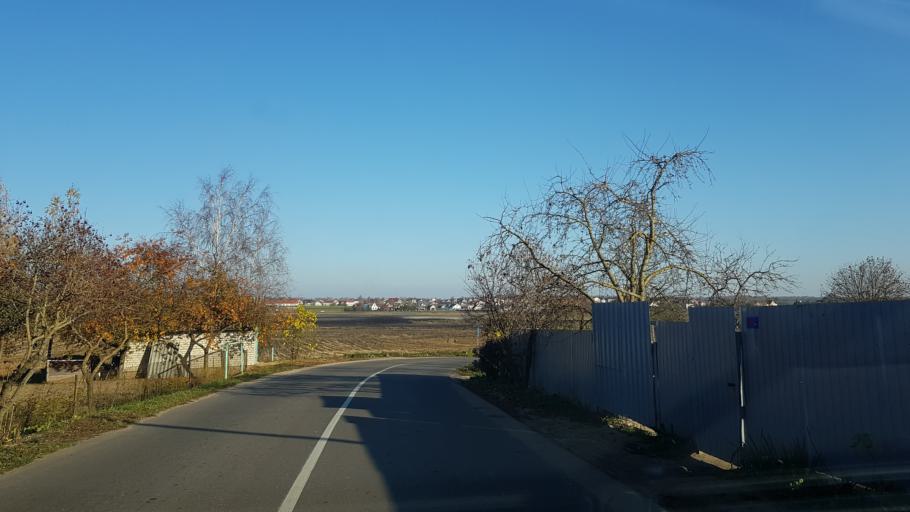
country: BY
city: Fanipol
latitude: 53.7214
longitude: 27.3022
